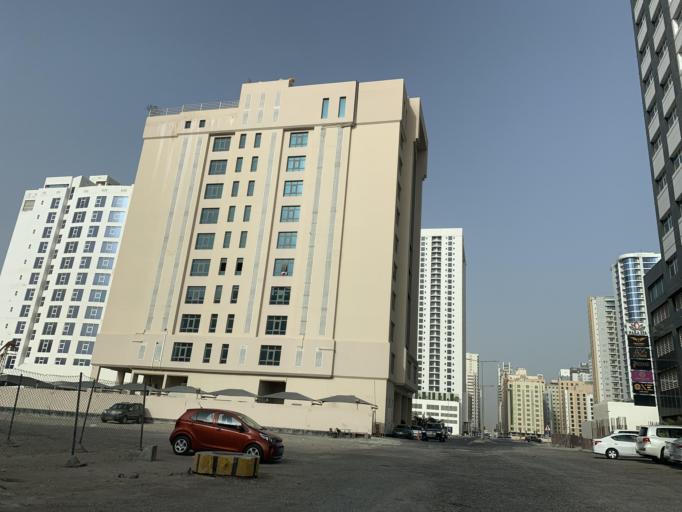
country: BH
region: Manama
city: Manama
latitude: 26.2210
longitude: 50.6143
